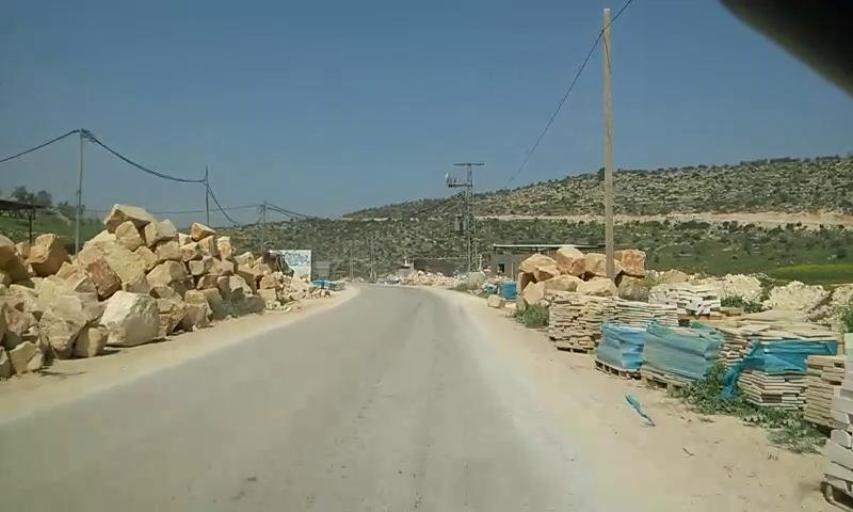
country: PS
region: West Bank
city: Az Zababidah
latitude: 32.4019
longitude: 35.3176
